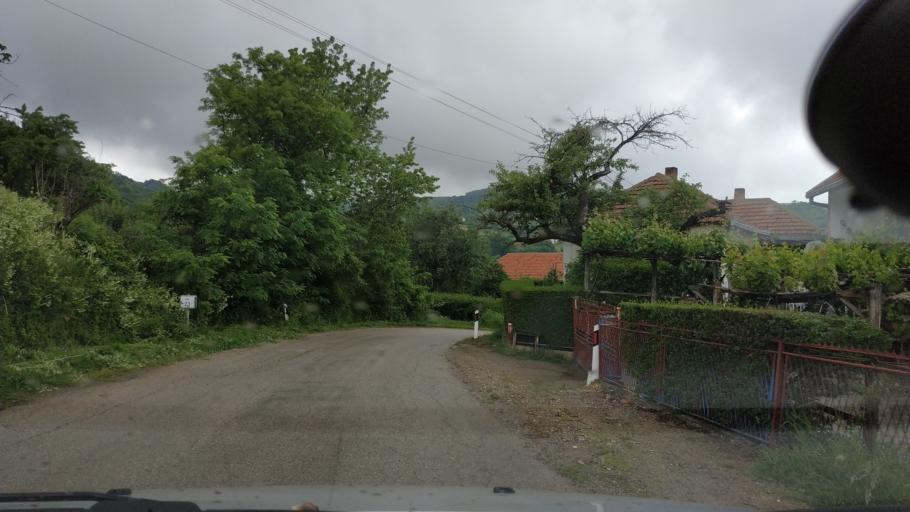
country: RS
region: Central Serbia
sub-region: Toplicki Okrug
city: Prokuplje
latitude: 43.3971
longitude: 21.5550
